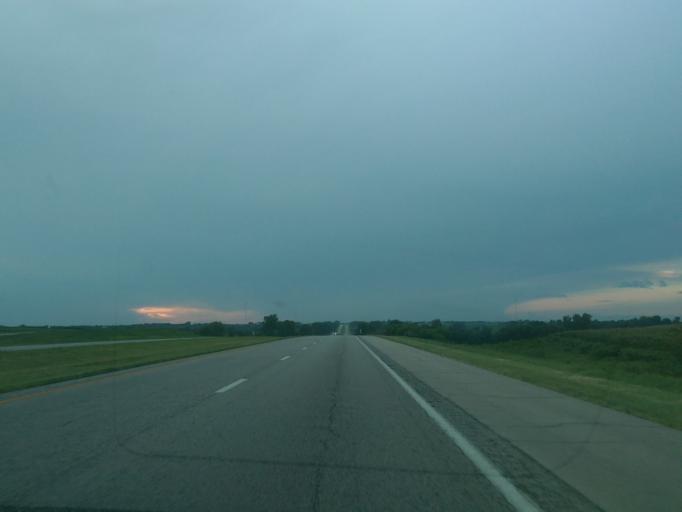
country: US
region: Missouri
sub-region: Holt County
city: Oregon
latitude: 40.0547
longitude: -95.1560
